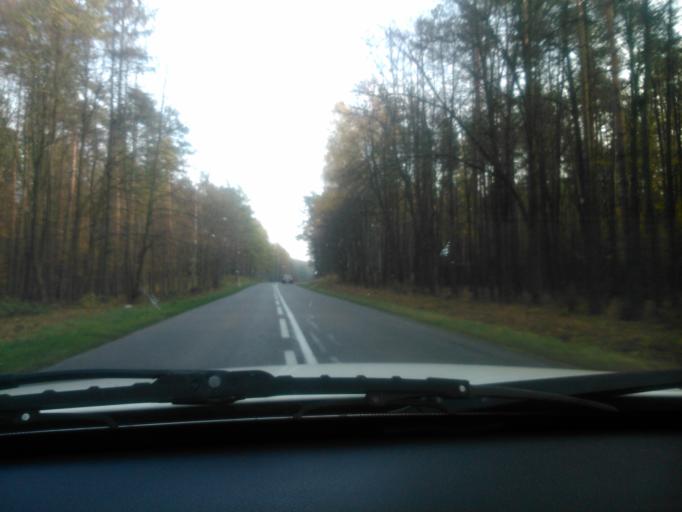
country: PL
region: Warmian-Masurian Voivodeship
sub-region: Powiat dzialdowski
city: Lidzbark
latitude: 53.2712
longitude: 19.8014
